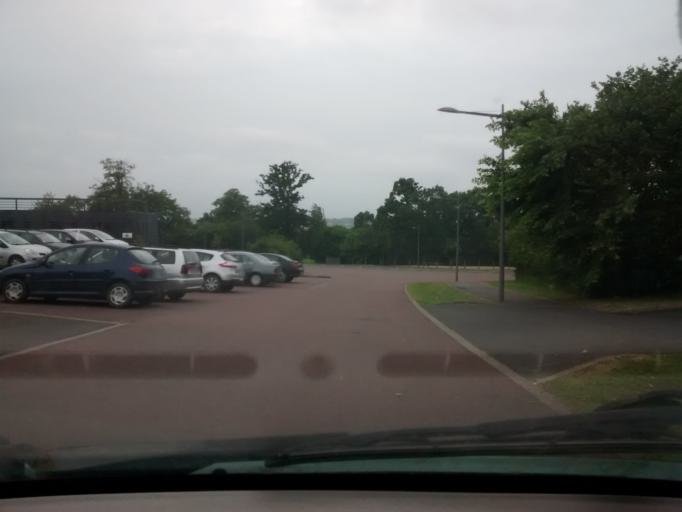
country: FR
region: Lower Normandy
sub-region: Departement de la Manche
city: Saint-Lo
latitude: 49.1037
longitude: -1.0782
